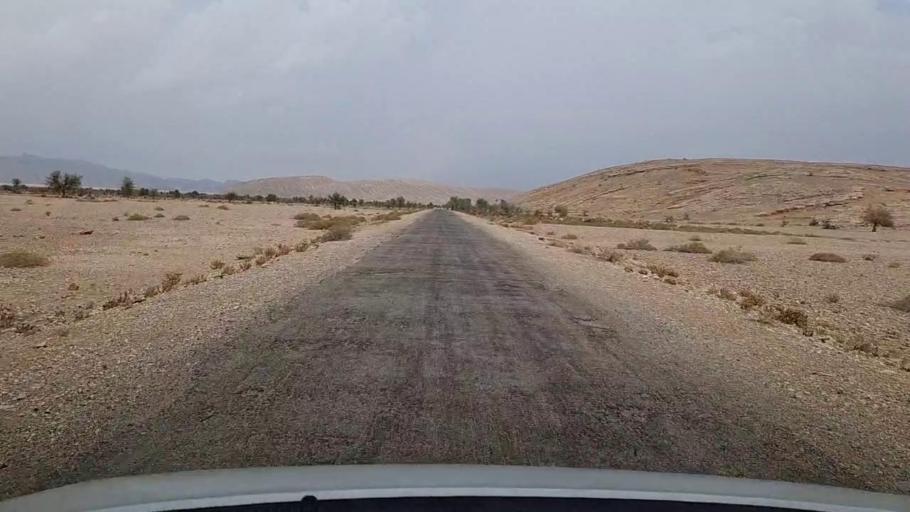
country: PK
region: Sindh
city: Sehwan
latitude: 26.2276
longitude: 67.7074
